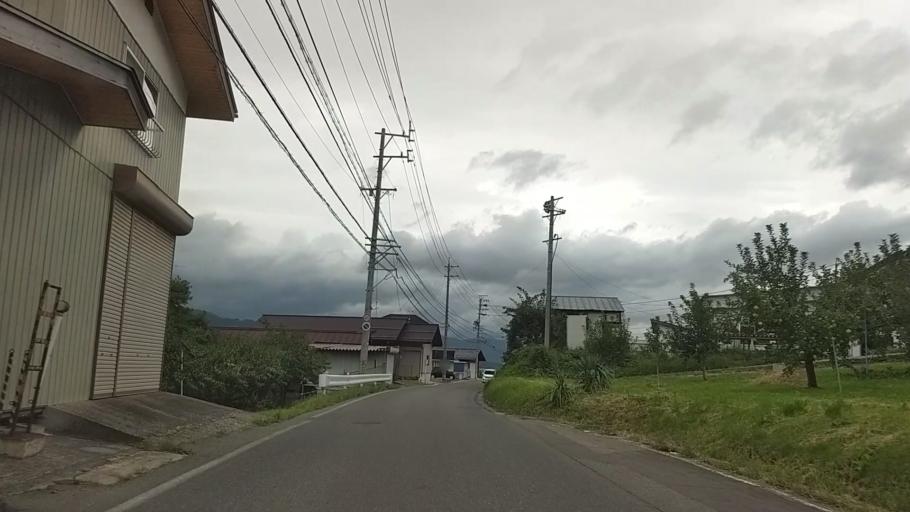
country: JP
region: Nagano
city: Iiyama
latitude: 36.8020
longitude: 138.3589
